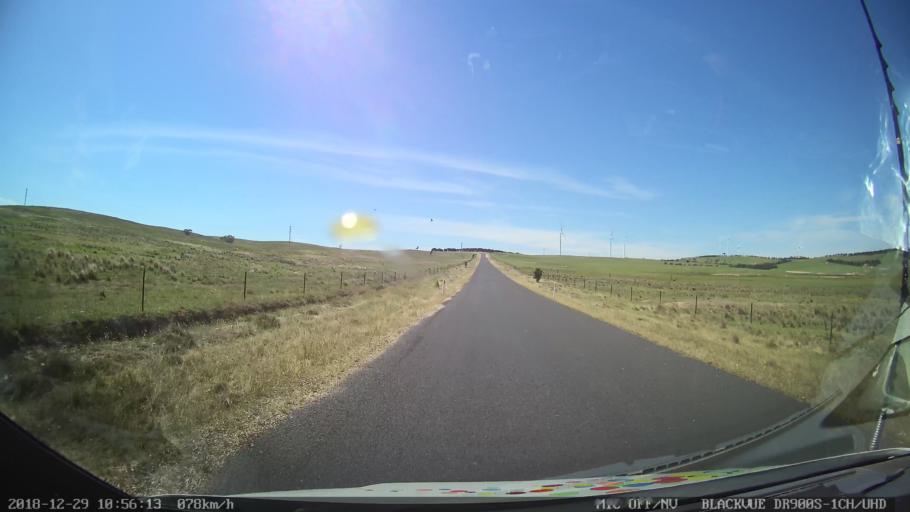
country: AU
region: New South Wales
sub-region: Palerang
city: Bungendore
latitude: -35.1316
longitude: 149.5372
